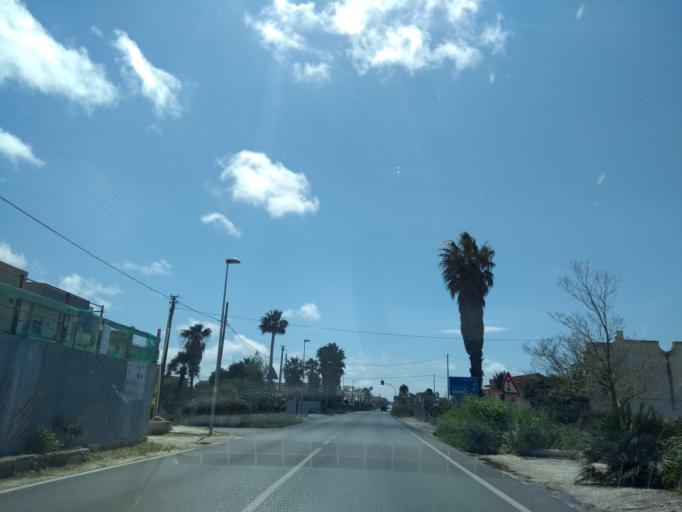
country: IT
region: Sicily
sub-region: Trapani
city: Marsala
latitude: 37.8522
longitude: 12.5128
